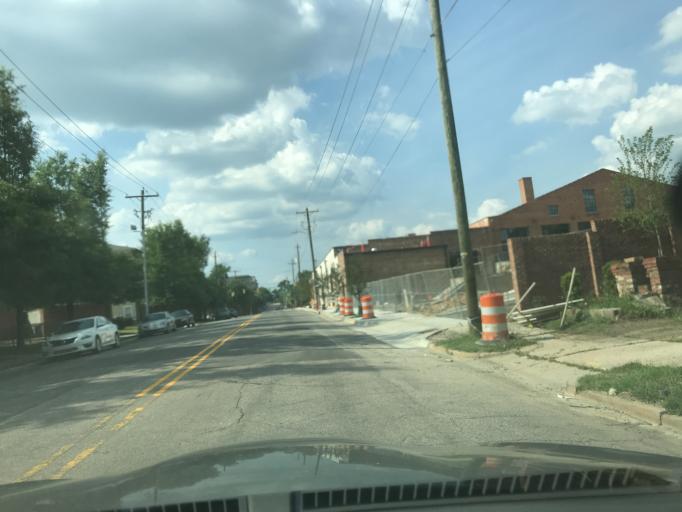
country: US
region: North Carolina
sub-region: Wake County
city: Raleigh
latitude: 35.7743
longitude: -78.6325
